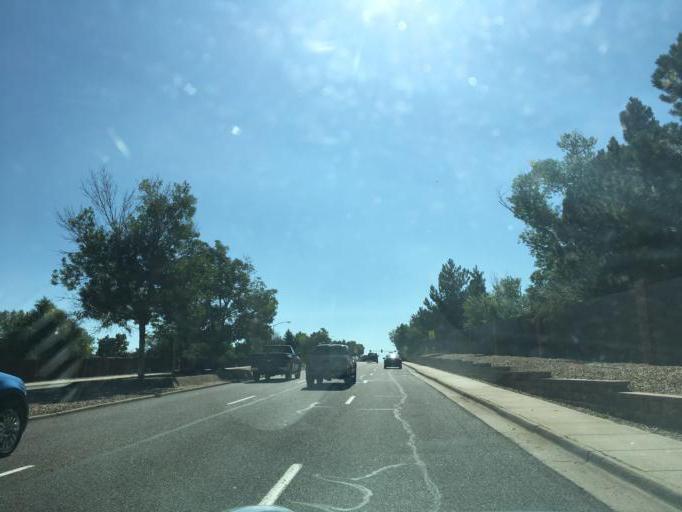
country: US
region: Colorado
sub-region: Arapahoe County
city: Dove Valley
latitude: 39.6303
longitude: -104.8037
